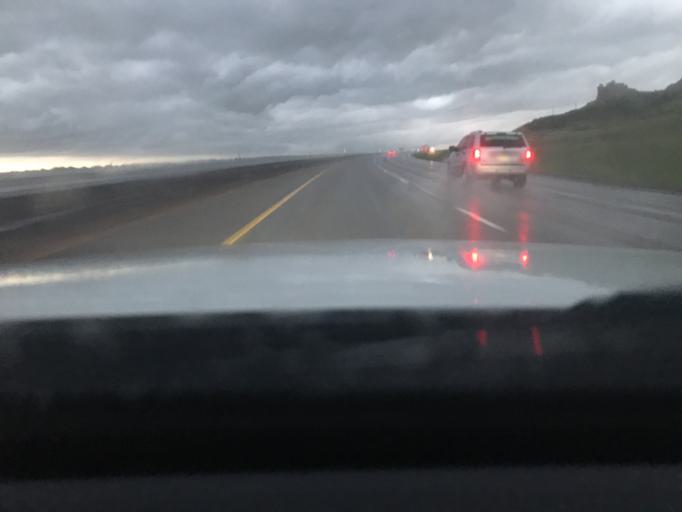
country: US
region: Wyoming
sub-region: Platte County
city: Wheatland
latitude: 41.7657
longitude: -104.8097
